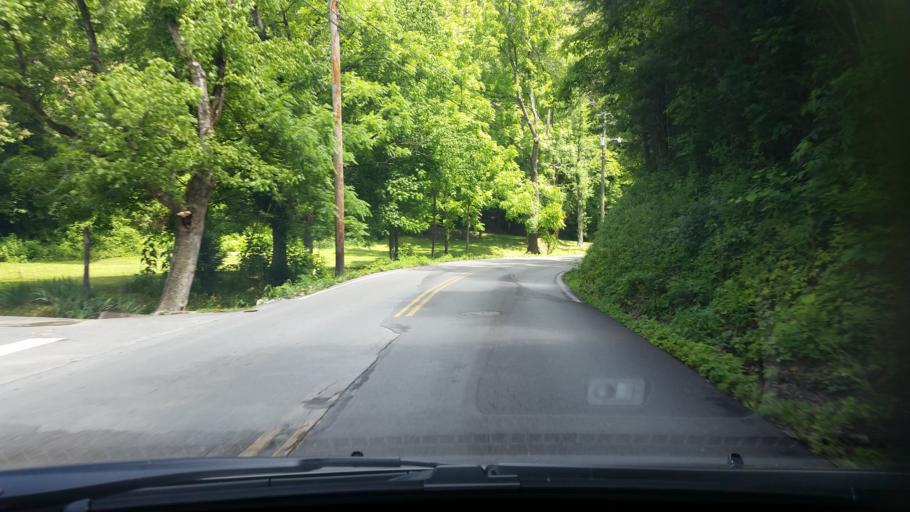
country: US
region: Tennessee
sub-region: Sevier County
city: Gatlinburg
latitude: 35.7422
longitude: -83.4594
